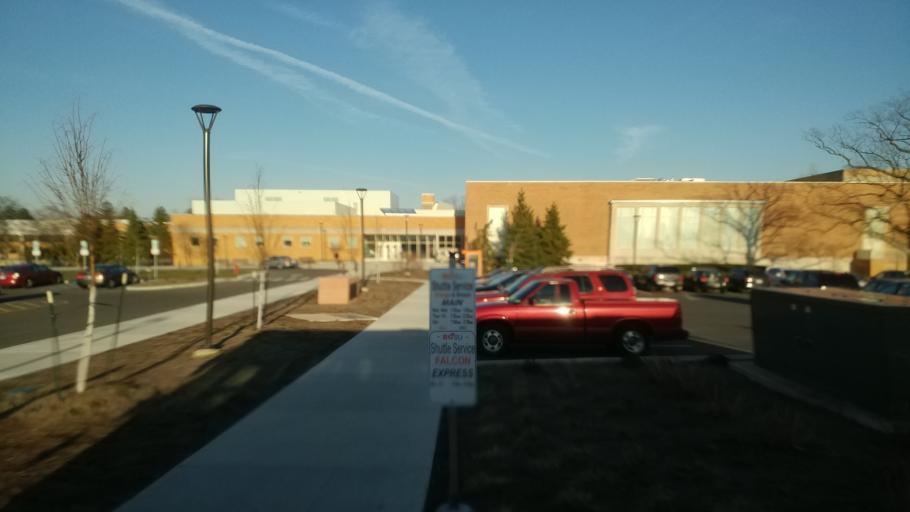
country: US
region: Ohio
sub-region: Wood County
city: Bowling Green
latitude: 41.3774
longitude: -83.6420
